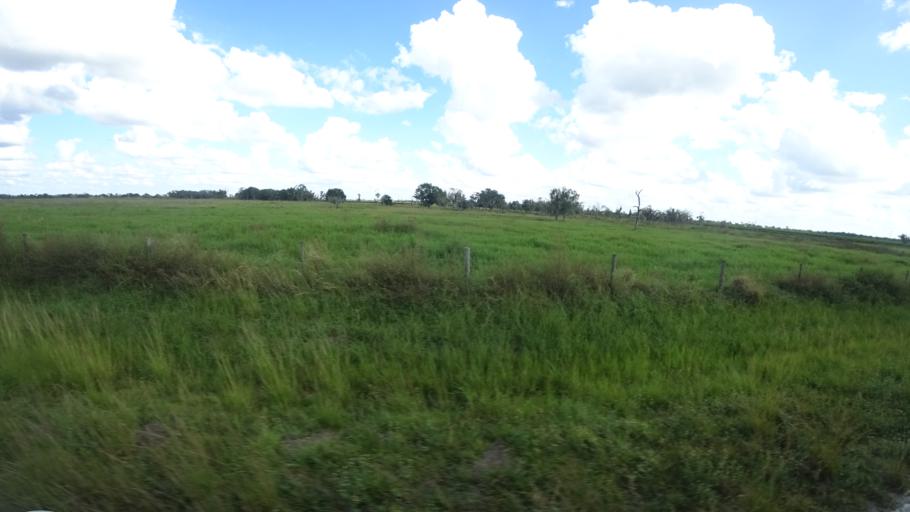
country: US
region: Florida
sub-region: DeSoto County
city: Nocatee
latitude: 27.2845
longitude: -82.1134
